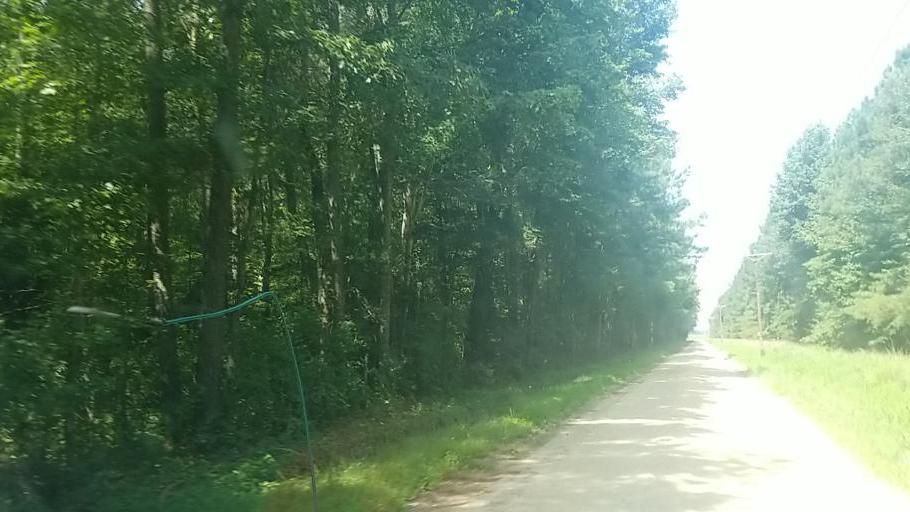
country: US
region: Maryland
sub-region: Caroline County
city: Denton
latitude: 38.8699
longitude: -75.7419
